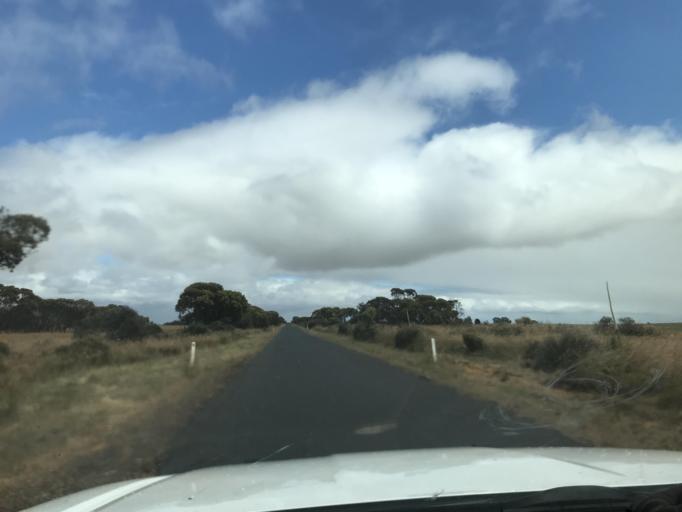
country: AU
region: South Australia
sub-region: Tatiara
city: Bordertown
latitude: -36.1372
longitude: 141.2003
